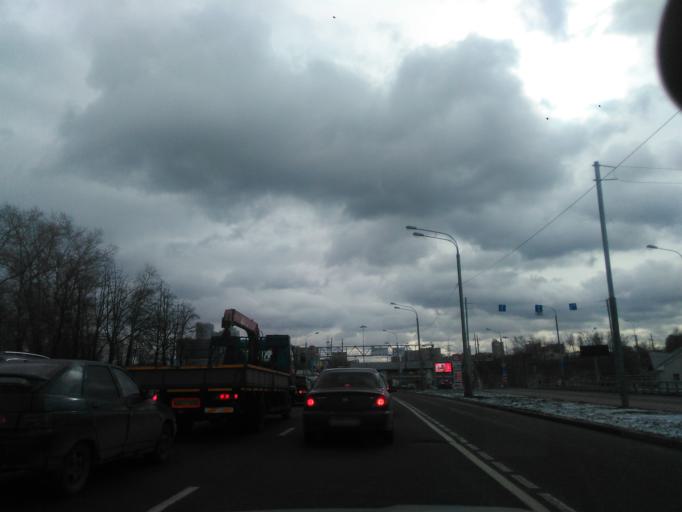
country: RU
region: Moscow
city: Pokrovskoye-Streshnevo
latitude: 55.8216
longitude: 37.4444
